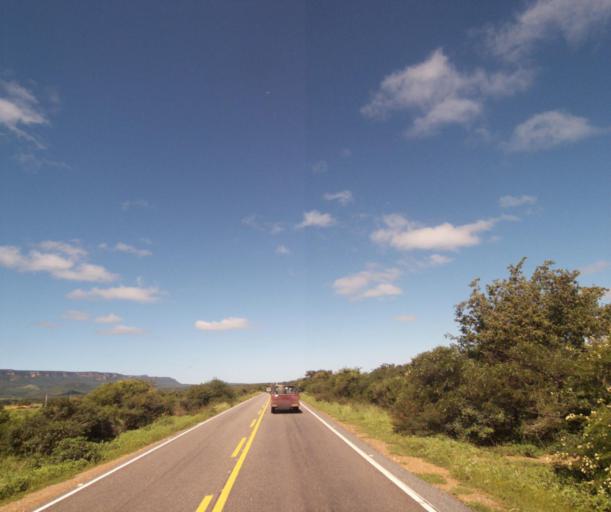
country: BR
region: Bahia
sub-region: Palmas De Monte Alto
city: Palmas de Monte Alto
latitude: -14.2416
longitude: -43.0640
